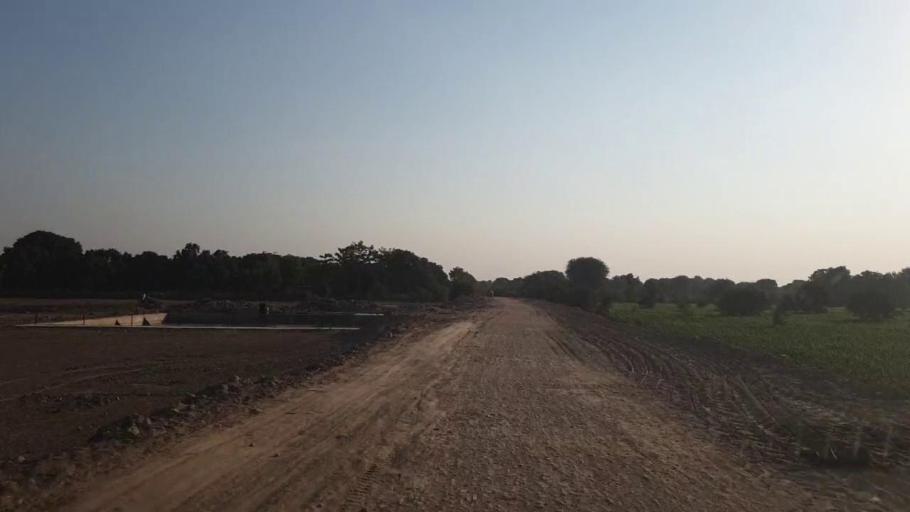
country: PK
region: Sindh
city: Mirpur Khas
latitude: 25.4186
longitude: 68.9064
